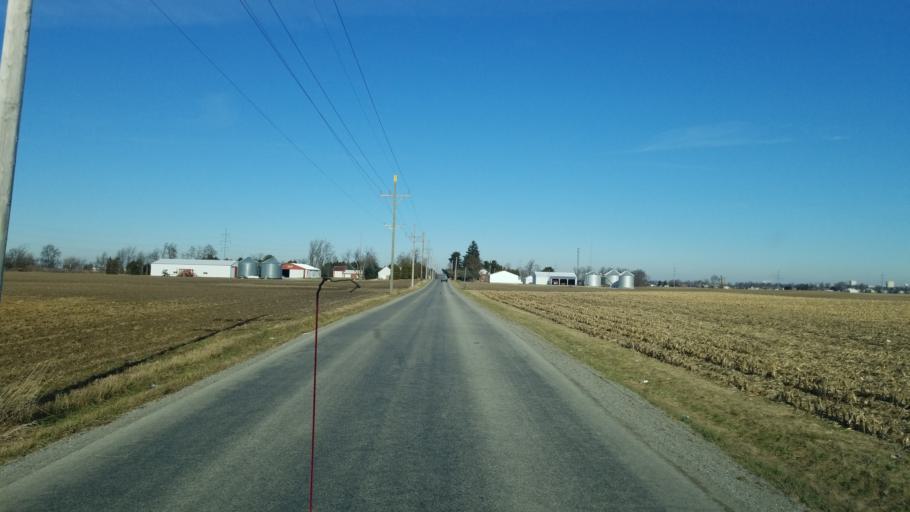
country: US
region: Ohio
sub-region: Putnam County
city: Leipsic
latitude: 41.0757
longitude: -83.9963
